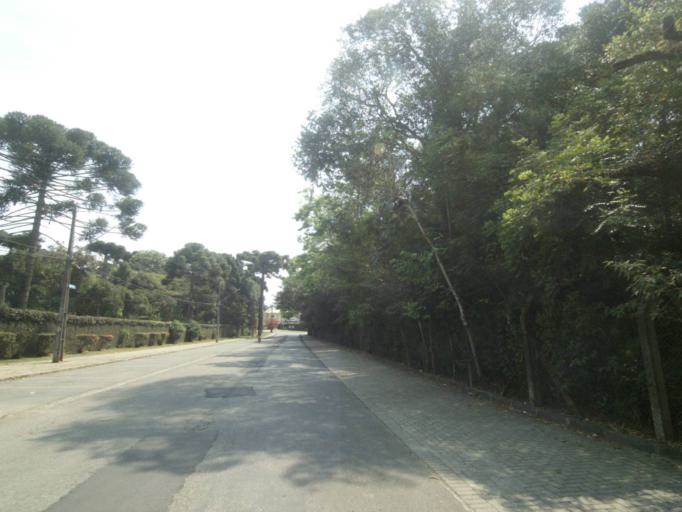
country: BR
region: Parana
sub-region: Sao Jose Dos Pinhais
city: Sao Jose dos Pinhais
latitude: -25.4885
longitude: -49.2096
